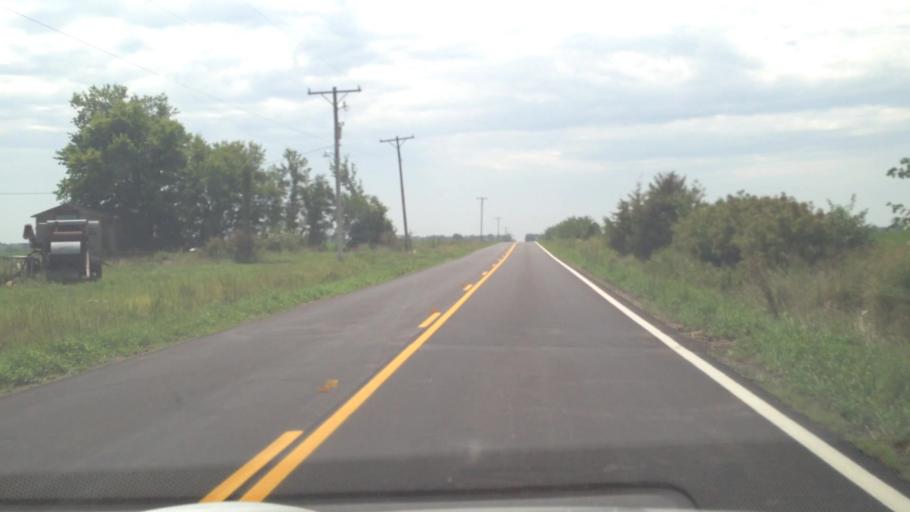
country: US
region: Kansas
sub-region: Crawford County
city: Girard
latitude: 37.6500
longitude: -94.9698
